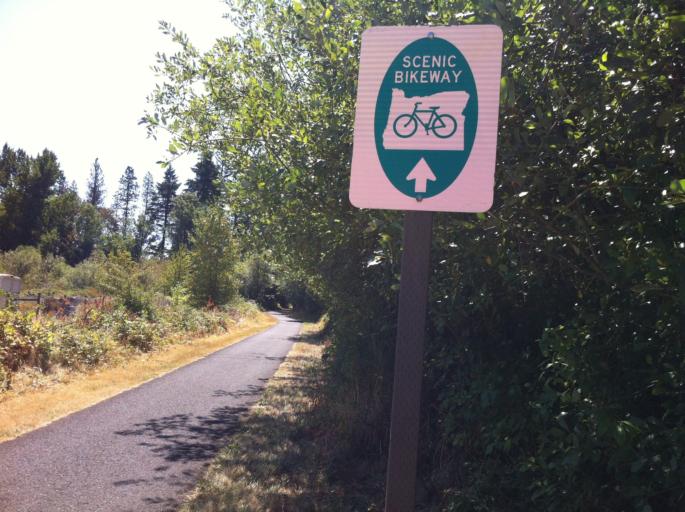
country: US
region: Oregon
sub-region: Washington County
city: Banks
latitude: 45.6647
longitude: -123.1634
